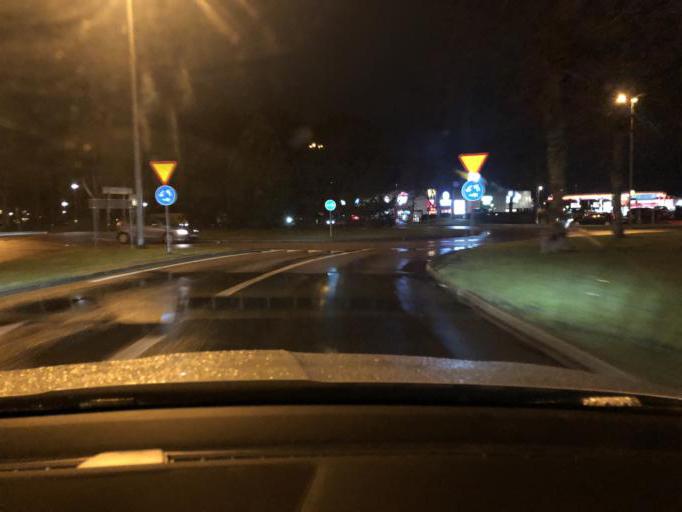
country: SE
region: Joenkoeping
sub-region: Jonkopings Kommun
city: Jonkoping
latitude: 57.7720
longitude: 14.1998
